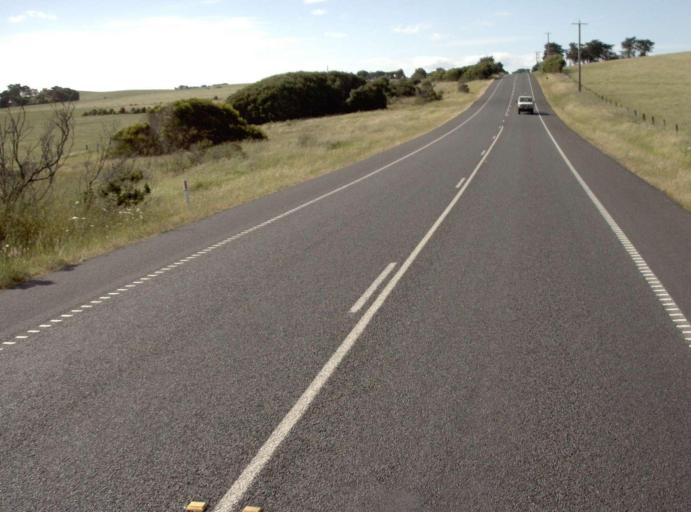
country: AU
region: Victoria
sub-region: Bass Coast
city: North Wonthaggi
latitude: -38.5381
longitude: 145.4569
